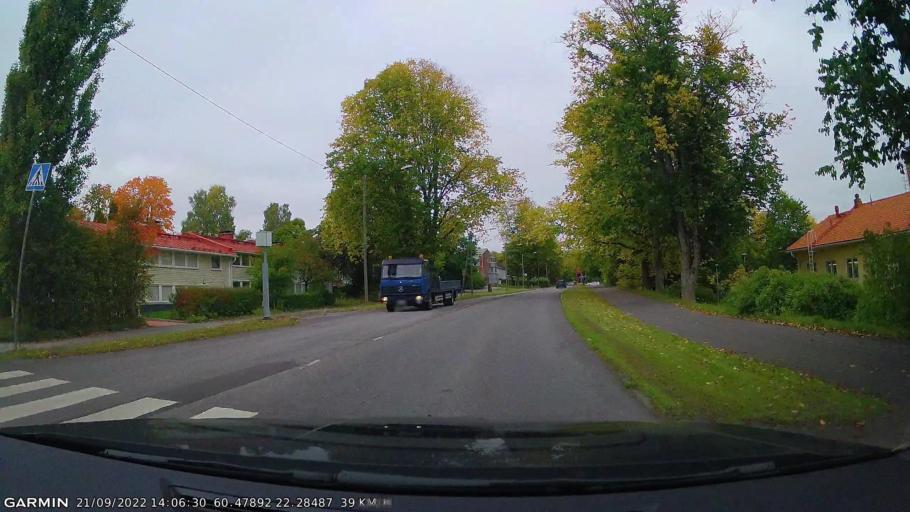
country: FI
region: Varsinais-Suomi
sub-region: Turku
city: Turku
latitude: 60.4789
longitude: 22.2847
